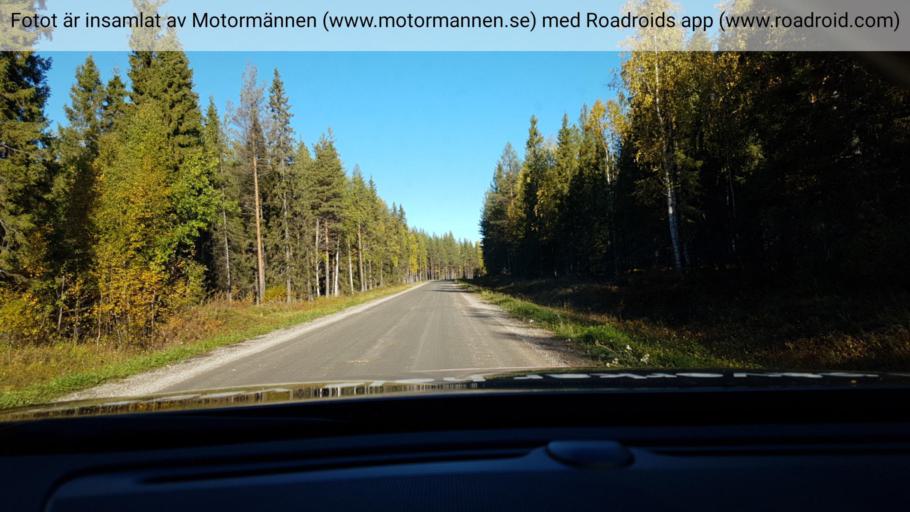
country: SE
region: Norrbotten
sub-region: Alvsbyns Kommun
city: AElvsbyn
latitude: 66.2645
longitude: 21.1298
